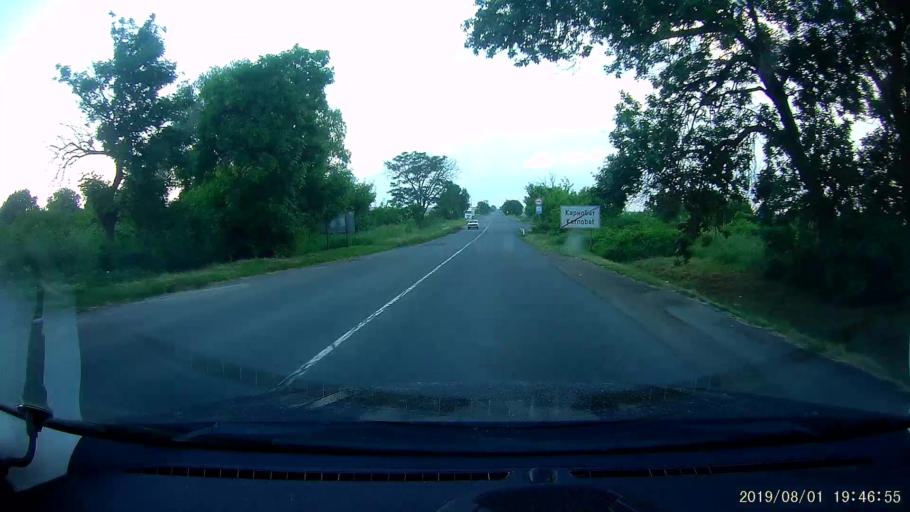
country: BG
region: Burgas
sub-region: Obshtina Karnobat
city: Karnobat
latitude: 42.6502
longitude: 26.9656
